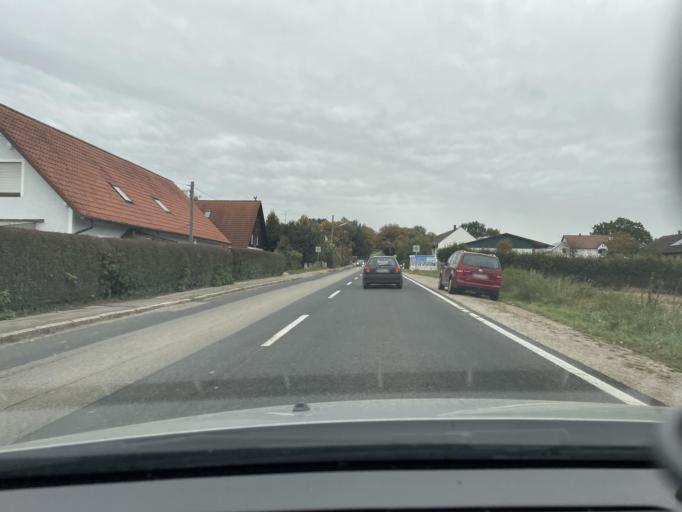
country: DE
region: Bavaria
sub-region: Upper Bavaria
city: Fahrenzhausen
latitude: 48.3801
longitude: 11.5407
